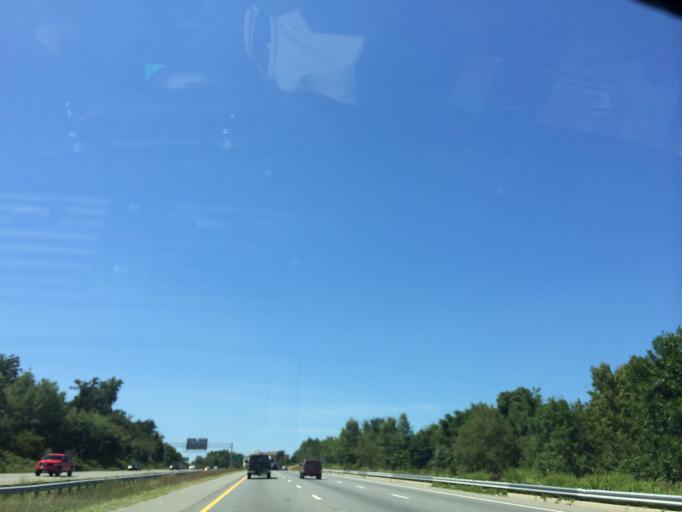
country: US
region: Maryland
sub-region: Howard County
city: West Elkridge
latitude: 39.2038
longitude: -76.7741
